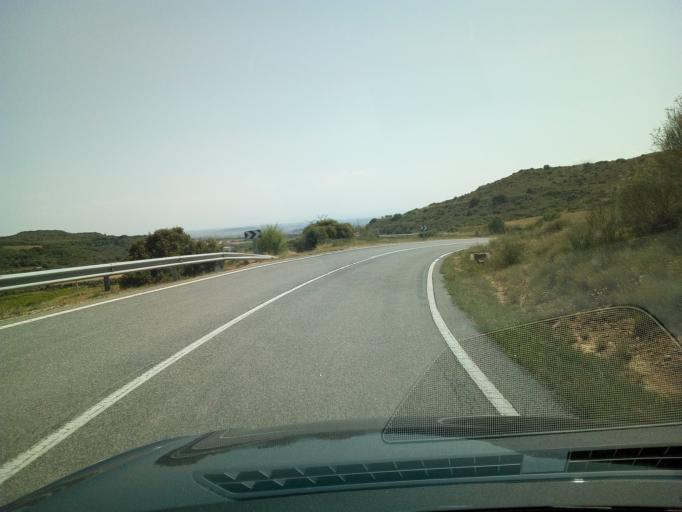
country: ES
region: Navarre
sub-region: Provincia de Navarra
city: San Martin de Unx
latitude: 42.5106
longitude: -1.5655
